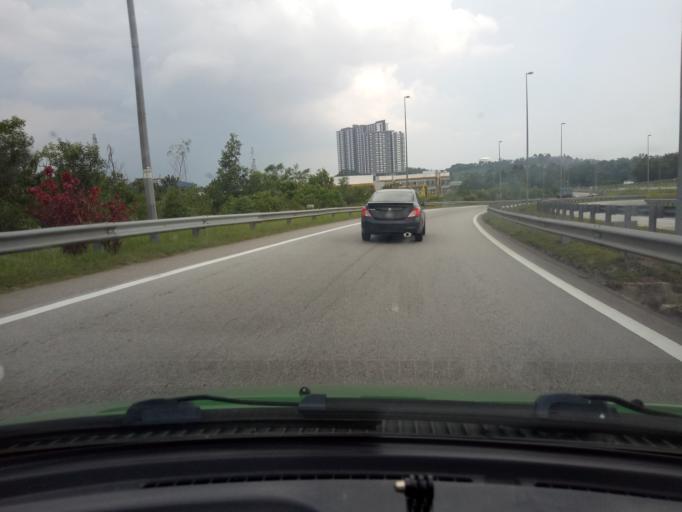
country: MY
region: Selangor
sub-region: Hulu Langat
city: Semenyih
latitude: 2.9704
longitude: 101.8350
